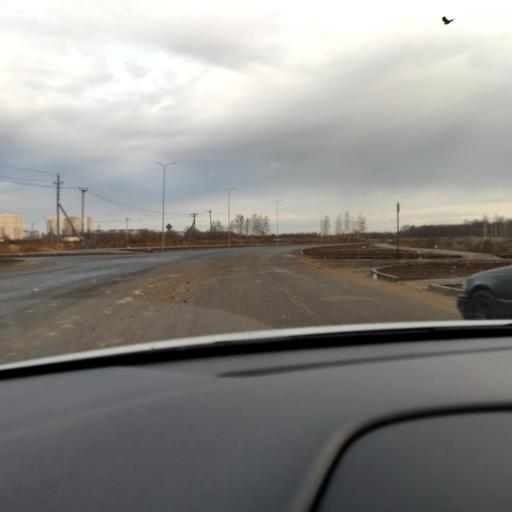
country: RU
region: Tatarstan
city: Osinovo
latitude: 55.8607
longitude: 48.8991
